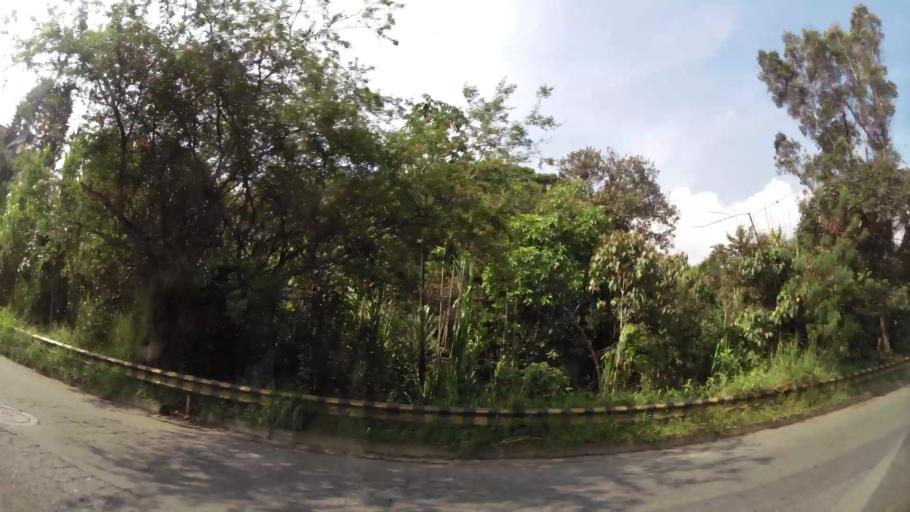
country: CO
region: Antioquia
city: La Estrella
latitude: 6.1706
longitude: -75.6312
